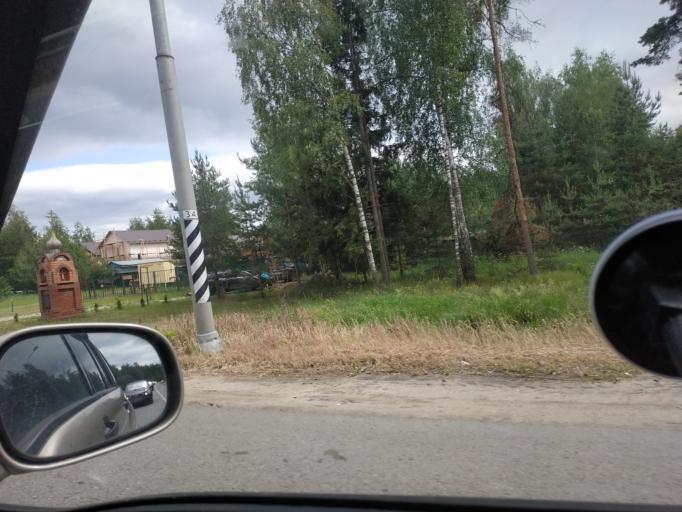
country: RU
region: Moskovskaya
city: Krasnoarmeysk
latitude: 56.0182
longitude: 38.1609
